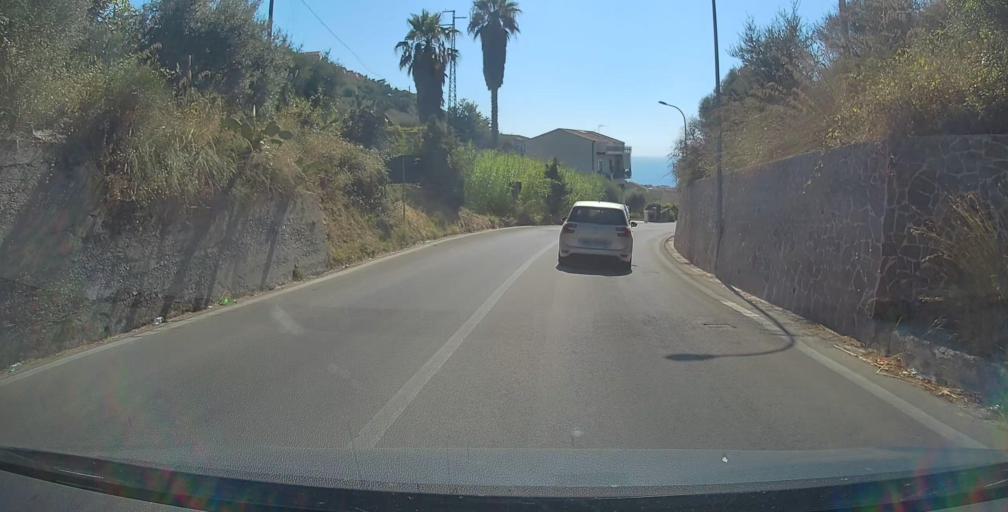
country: IT
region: Sicily
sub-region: Messina
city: Capo d'Orlando
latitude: 38.1570
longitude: 14.7514
